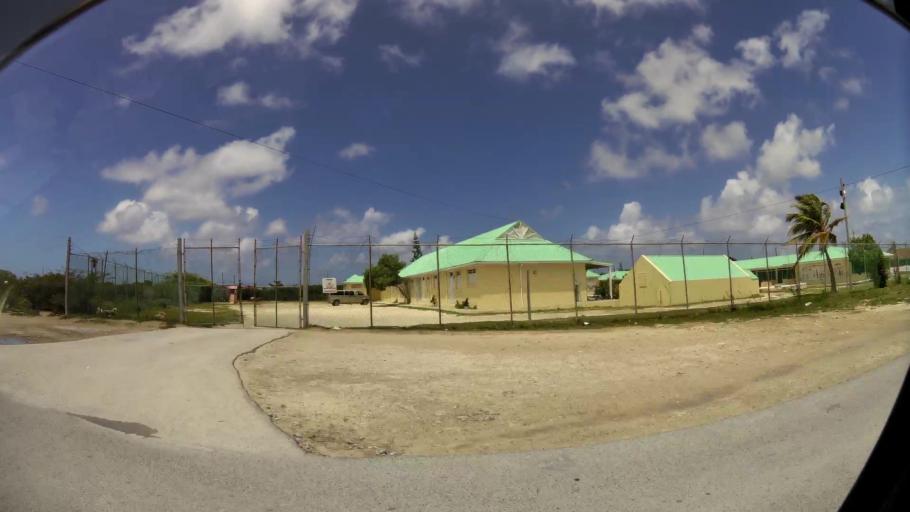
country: TC
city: Cockburn Town
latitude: 21.4567
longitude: -71.1404
